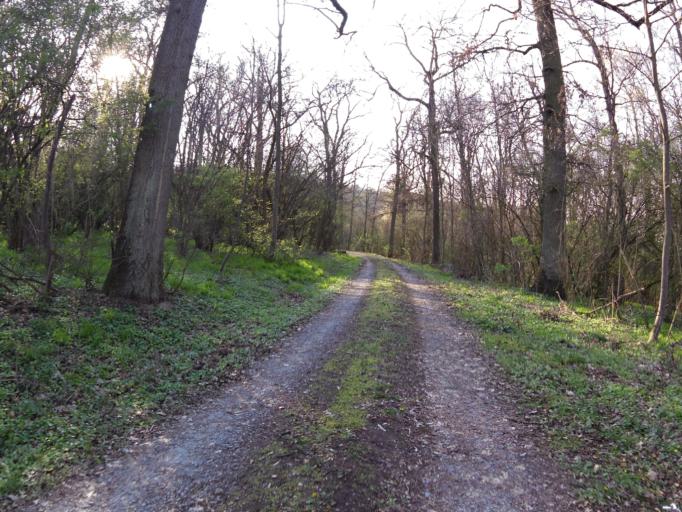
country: DE
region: Bavaria
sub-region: Regierungsbezirk Unterfranken
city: Rottendorf
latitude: 49.7751
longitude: 10.0477
